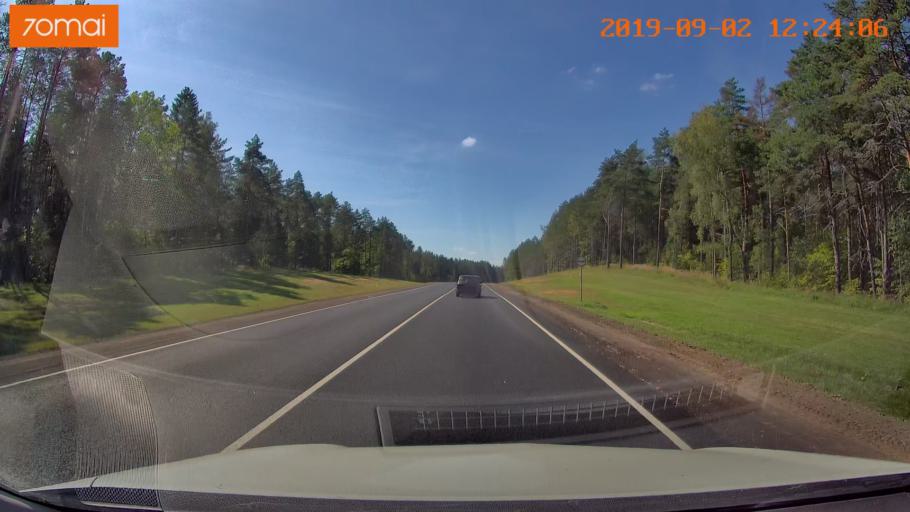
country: RU
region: Smolensk
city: Shumyachi
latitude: 53.8710
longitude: 32.6137
